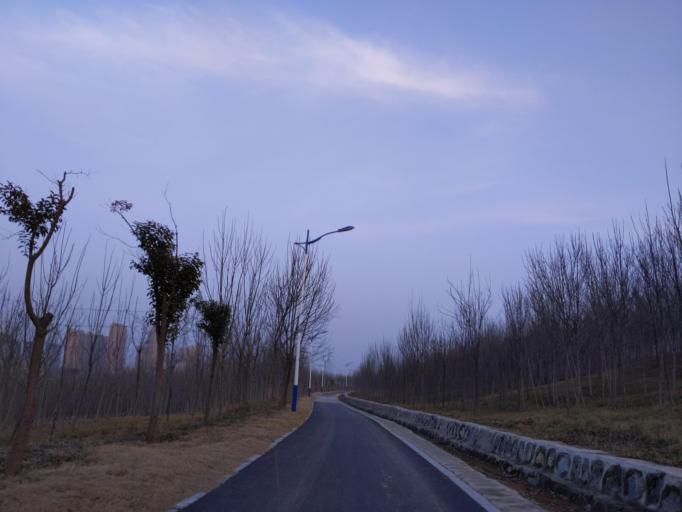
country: CN
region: Henan Sheng
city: Zhongyuanlu
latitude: 35.8184
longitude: 115.0508
